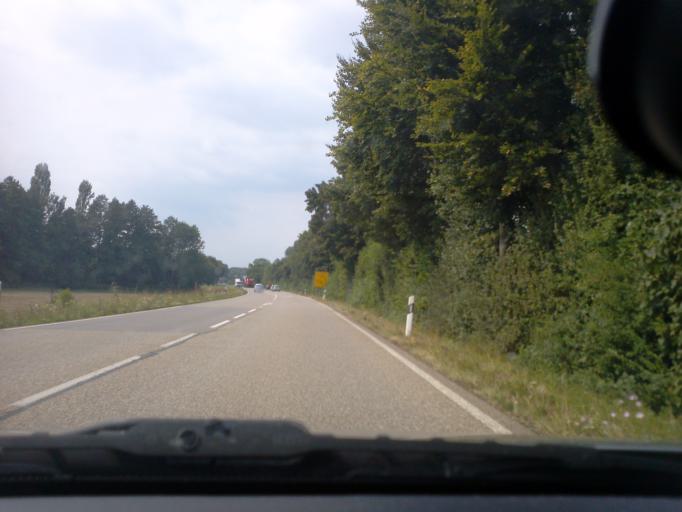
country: DE
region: Baden-Wuerttemberg
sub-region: Karlsruhe Region
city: Woessingen
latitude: 49.0214
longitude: 8.5923
